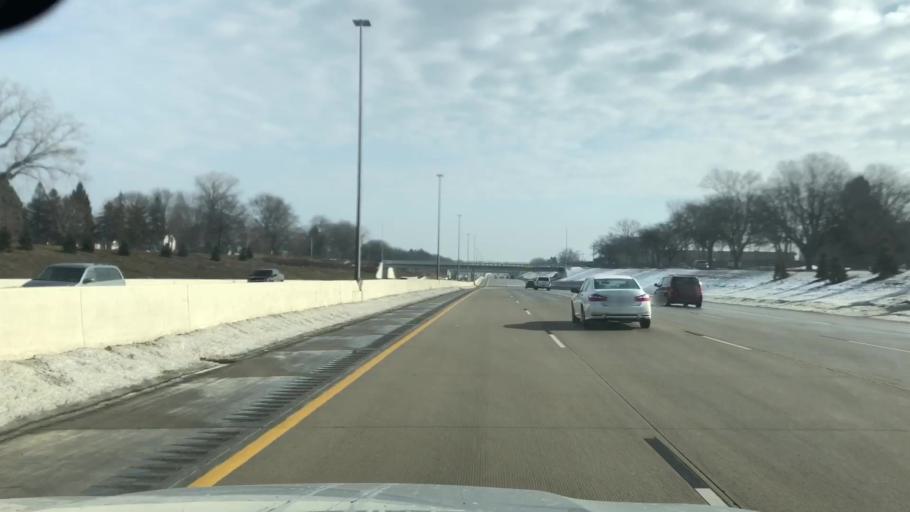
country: US
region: Michigan
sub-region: Wayne County
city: Livonia
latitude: 42.3819
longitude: -83.3959
